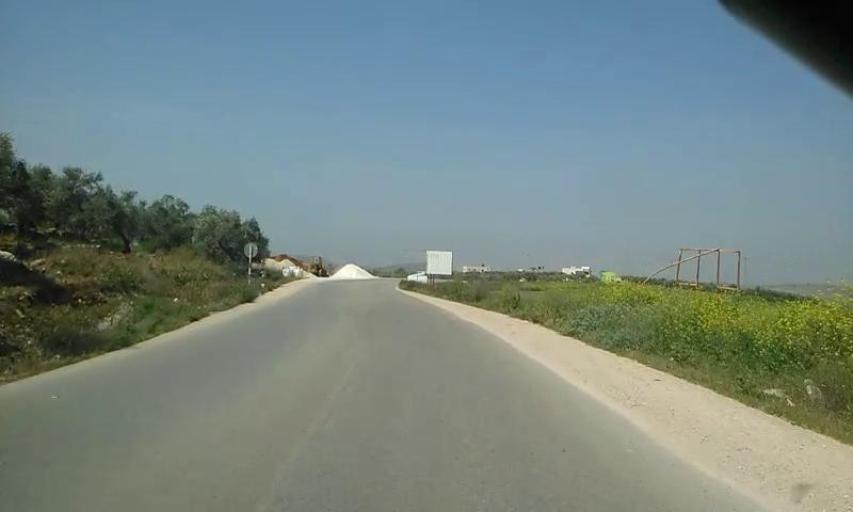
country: PS
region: West Bank
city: Az Zababidah
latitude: 32.3779
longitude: 35.3328
